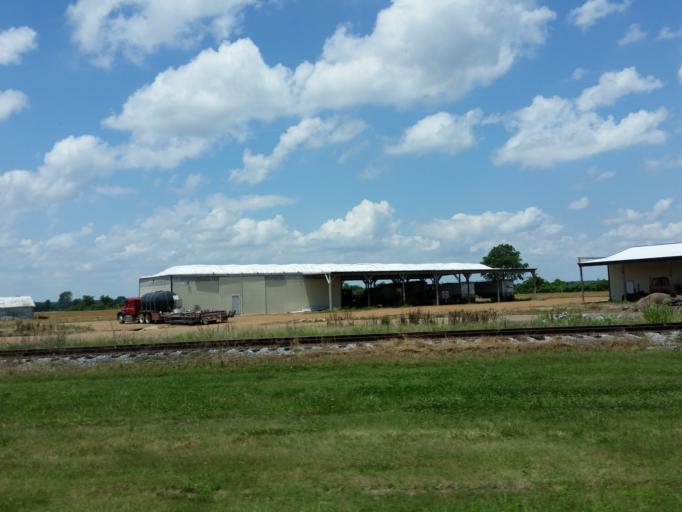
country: US
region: Tennessee
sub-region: Lake County
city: Tiptonville
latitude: 36.4832
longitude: -89.3751
